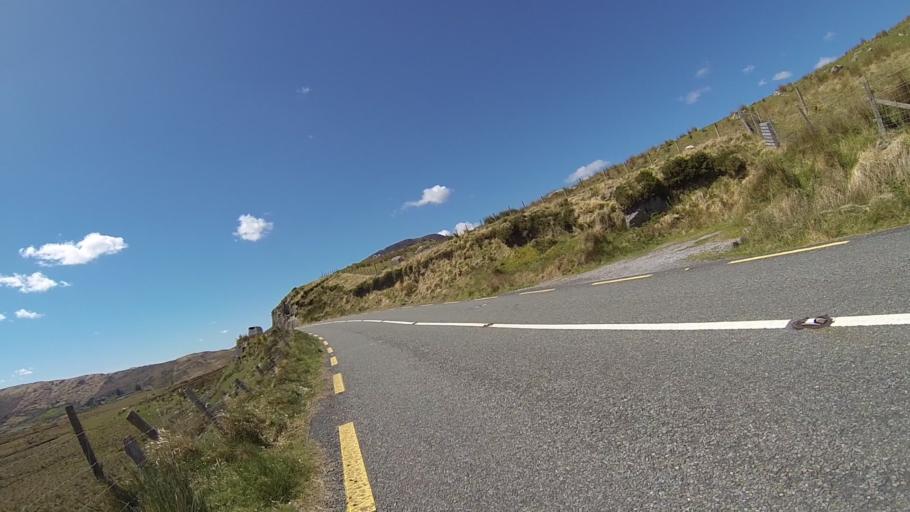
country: IE
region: Munster
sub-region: Ciarrai
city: Kenmare
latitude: 51.9277
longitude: -9.6444
